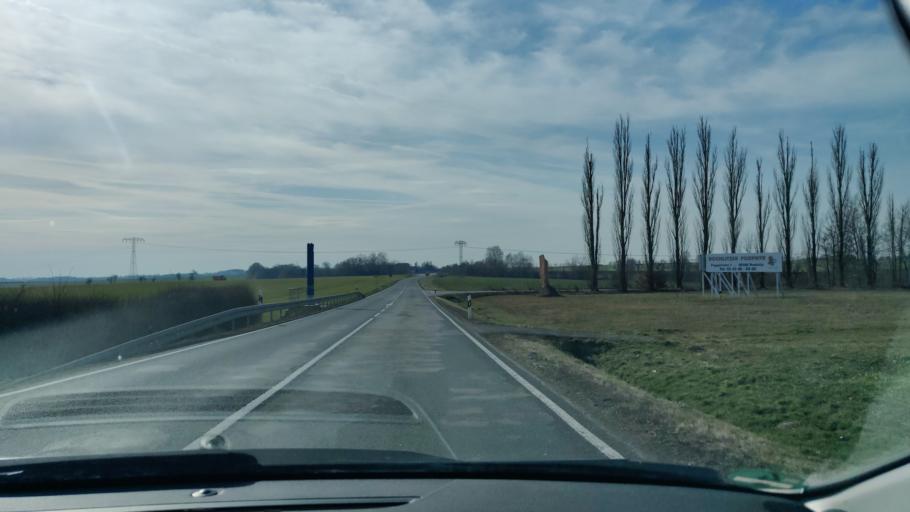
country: DE
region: Saxony
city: Wechselburg
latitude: 51.0228
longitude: 12.7467
